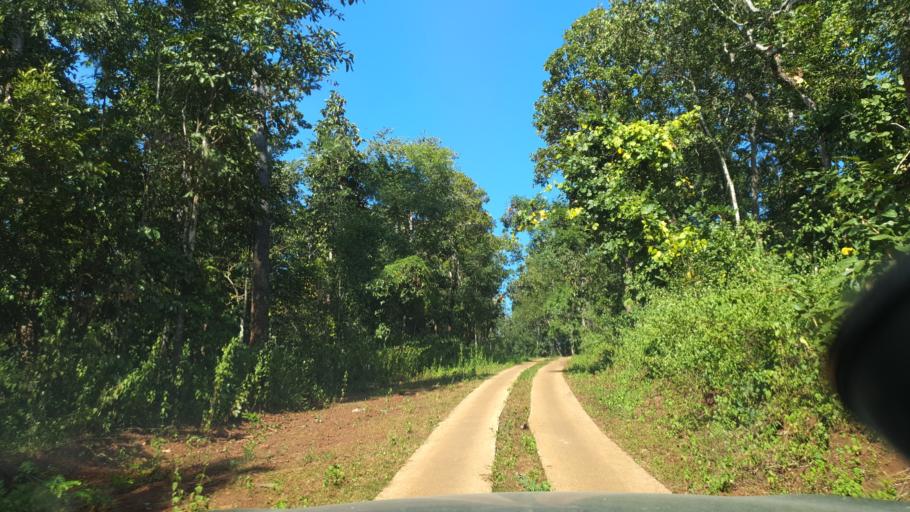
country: TH
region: Chiang Mai
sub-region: Amphoe Chiang Dao
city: Chiang Dao
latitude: 19.2985
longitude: 98.7157
